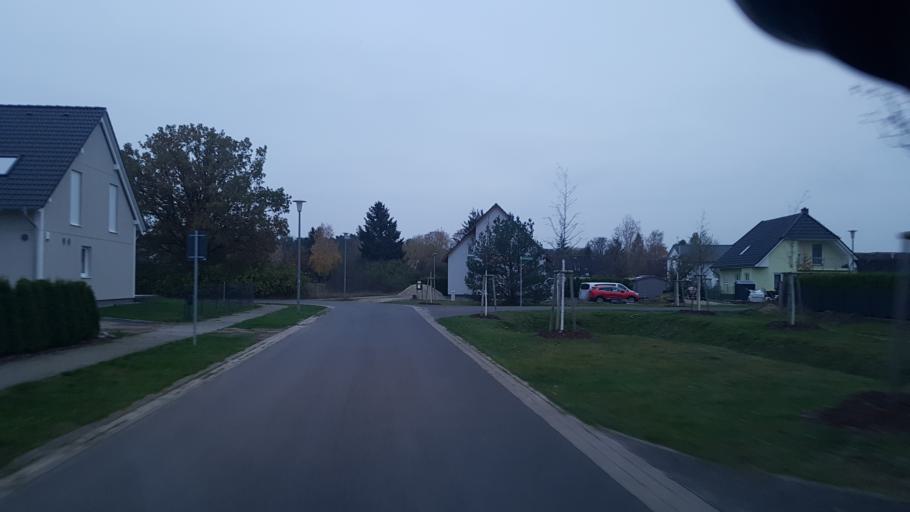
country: DE
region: Brandenburg
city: Nauen
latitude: 52.6855
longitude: 12.9406
